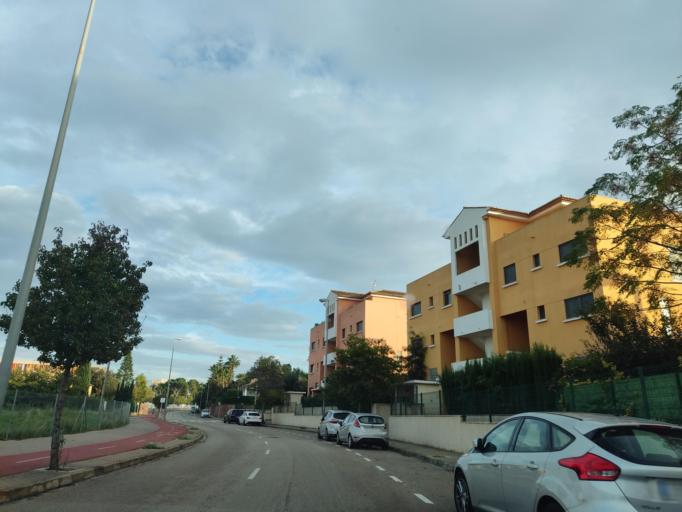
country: ES
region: Valencia
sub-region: Provincia de Alicante
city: Denia
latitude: 38.8331
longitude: 0.1122
